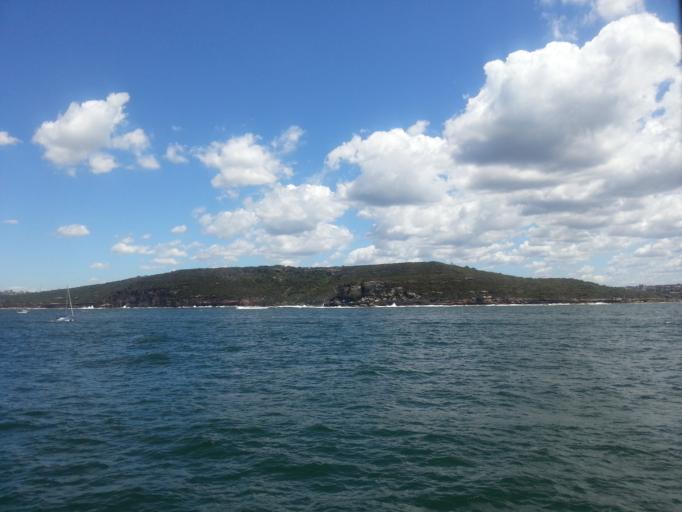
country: AU
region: New South Wales
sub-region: Manly Vale
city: Manly
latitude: -33.8157
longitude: 151.2796
